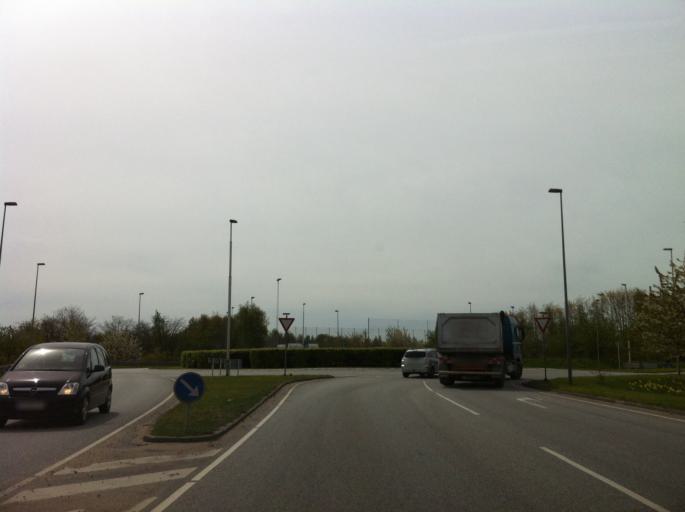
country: DK
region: Zealand
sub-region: Roskilde Kommune
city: Vindinge
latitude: 55.6409
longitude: 12.1155
